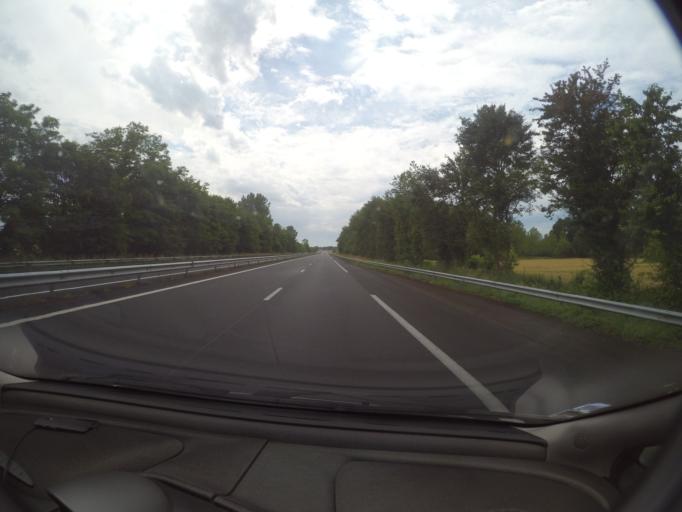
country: FR
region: Pays de la Loire
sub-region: Departement de Maine-et-Loire
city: Seiches-sur-le-Loir
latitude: 47.5929
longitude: -0.3189
